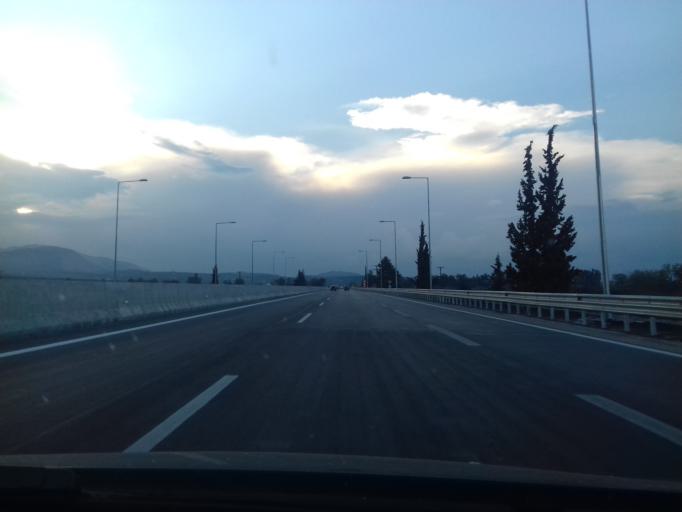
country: GR
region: West Greece
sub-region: Nomos Achaias
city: Temeni
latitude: 38.2229
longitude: 22.0996
